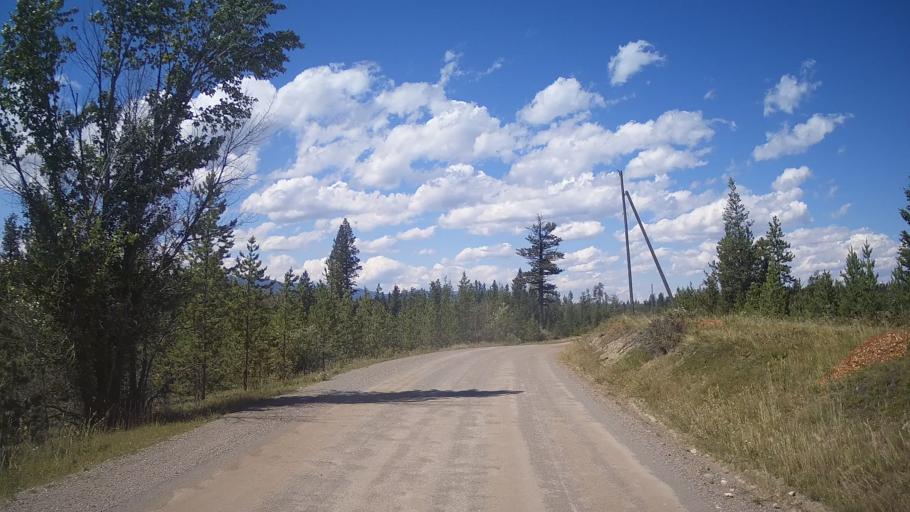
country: CA
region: British Columbia
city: Cache Creek
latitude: 51.2243
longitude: -121.6221
